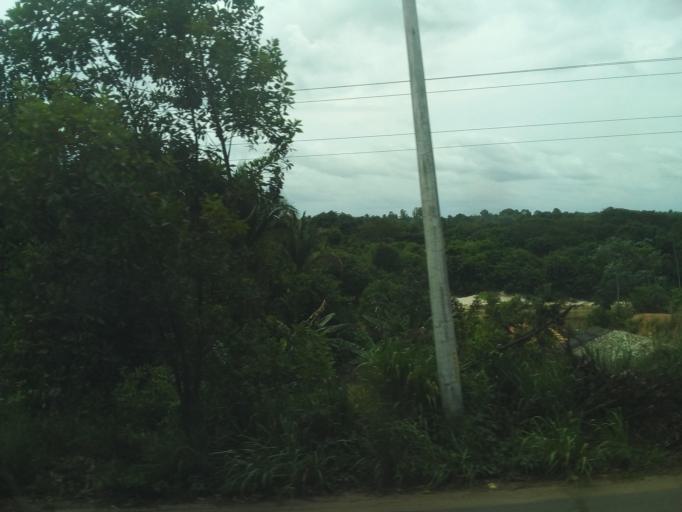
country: BR
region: Maranhao
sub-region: Santa Ines
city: Santa Ines
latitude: -3.6914
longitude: -45.9125
